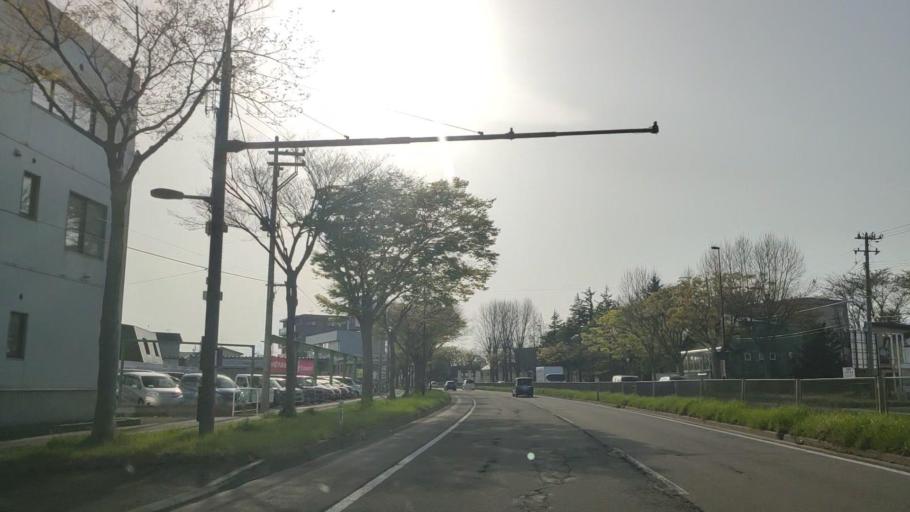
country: JP
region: Aomori
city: Aomori Shi
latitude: 40.8283
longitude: 140.7881
